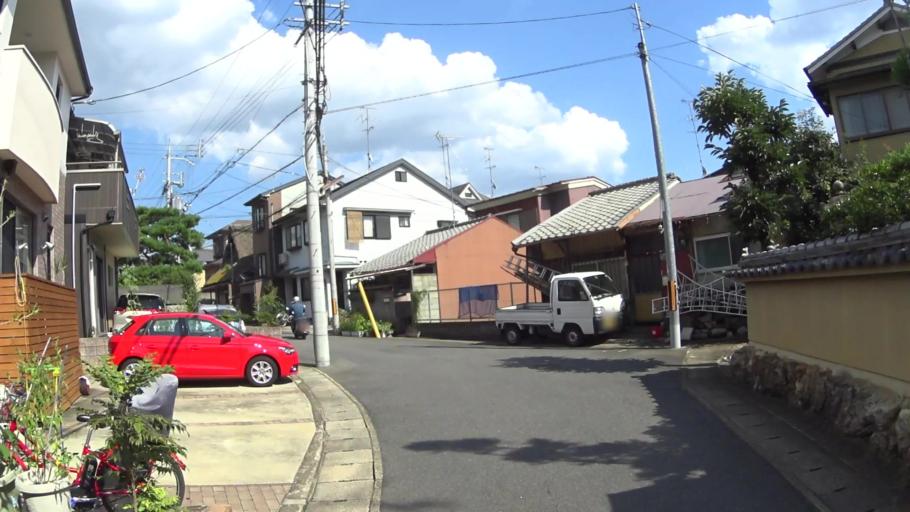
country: JP
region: Kyoto
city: Kyoto
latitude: 35.0286
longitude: 135.7057
